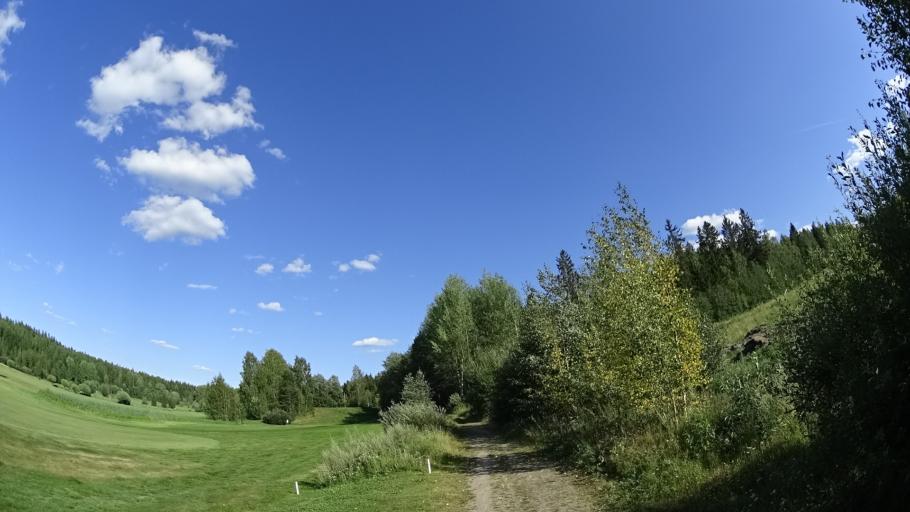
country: FI
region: Uusimaa
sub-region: Helsinki
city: Vihti
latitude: 60.3795
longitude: 24.3707
